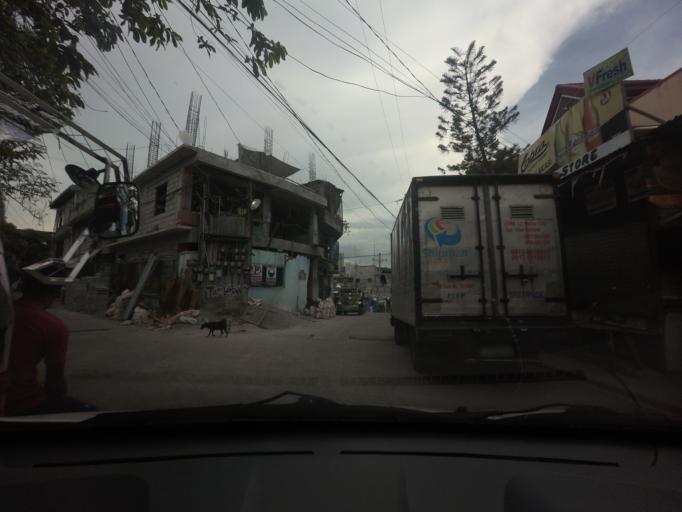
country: PH
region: Calabarzon
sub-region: Province of Rizal
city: Taguig
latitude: 14.5241
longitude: 121.0603
